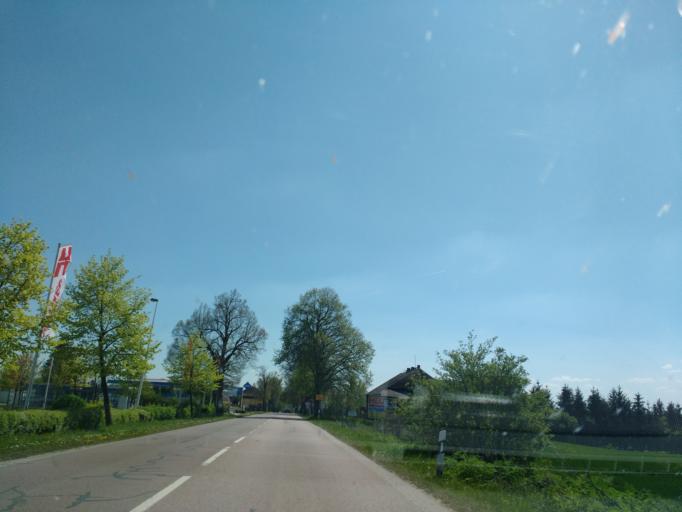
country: DE
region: Saxony-Anhalt
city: Theissen
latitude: 51.0701
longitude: 12.1209
